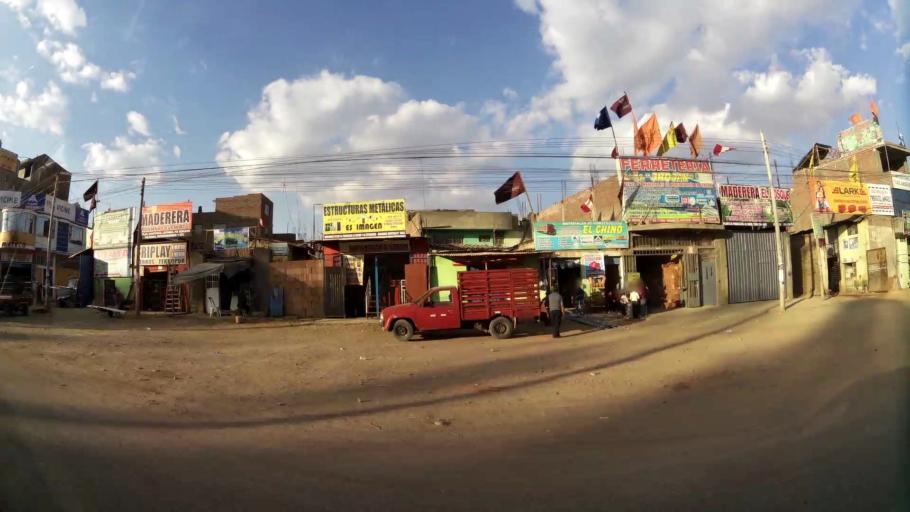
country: PE
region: Junin
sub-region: Provincia de Huancayo
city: Pilcomay
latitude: -12.0391
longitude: -75.2288
